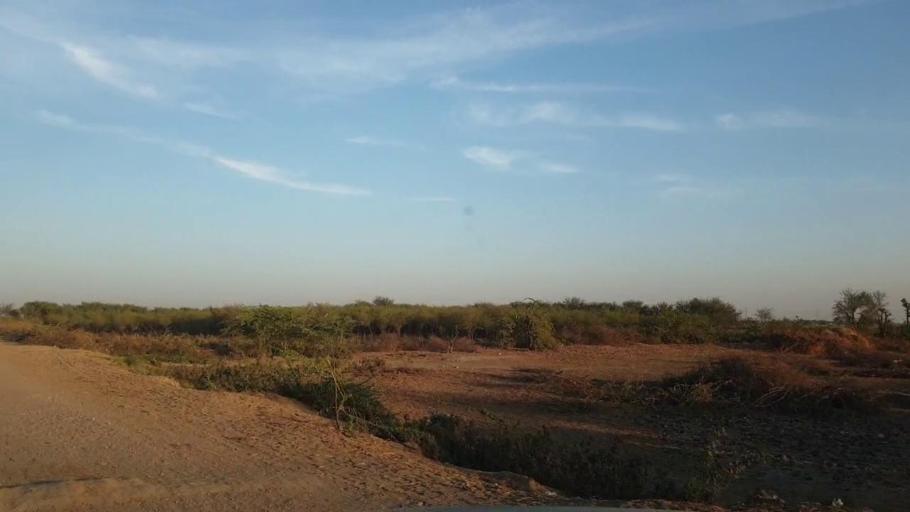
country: PK
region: Sindh
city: Kunri
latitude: 25.1289
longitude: 69.4286
